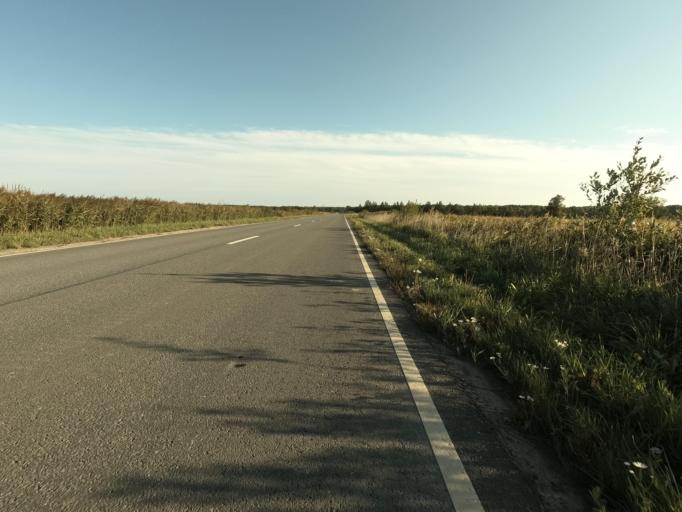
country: RU
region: St.-Petersburg
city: Sapernyy
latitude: 59.7335
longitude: 30.6574
